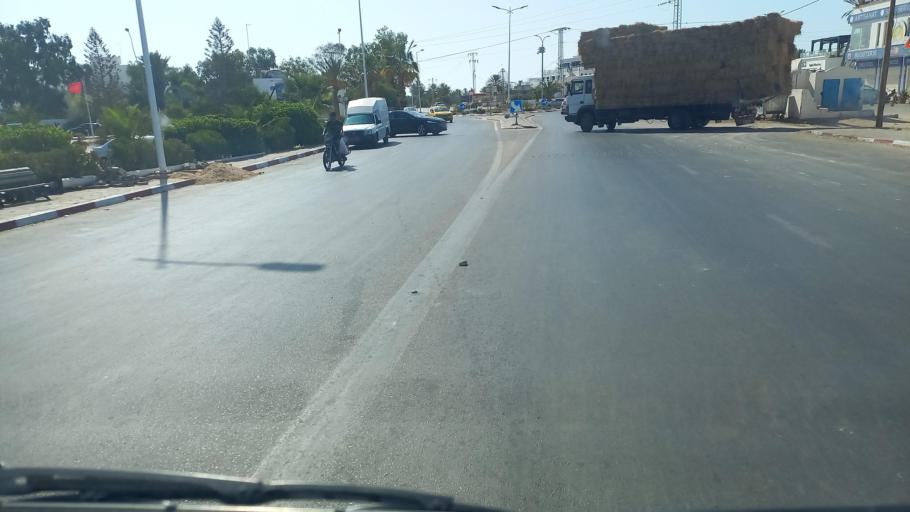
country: TN
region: Madanin
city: Midoun
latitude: 33.8396
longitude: 10.9924
